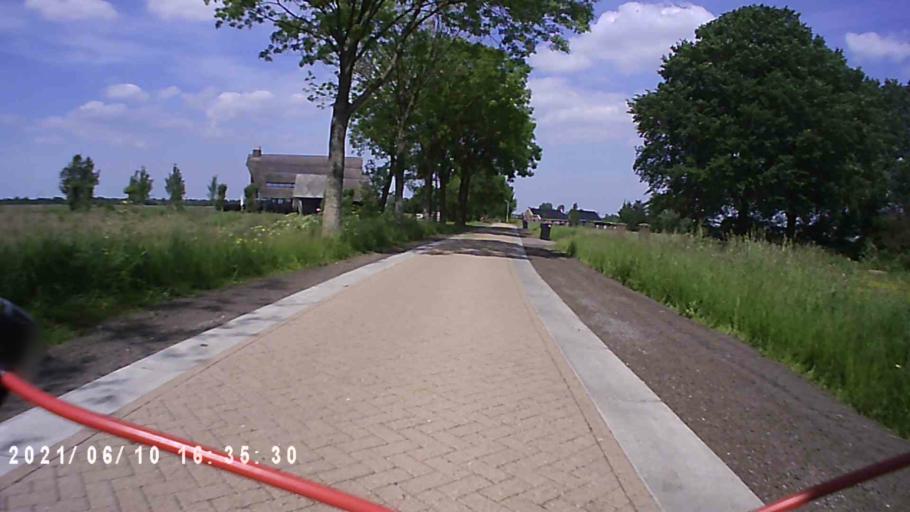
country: NL
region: Friesland
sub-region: Gemeente Achtkarspelen
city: Buitenpost
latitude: 53.2345
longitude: 6.1351
